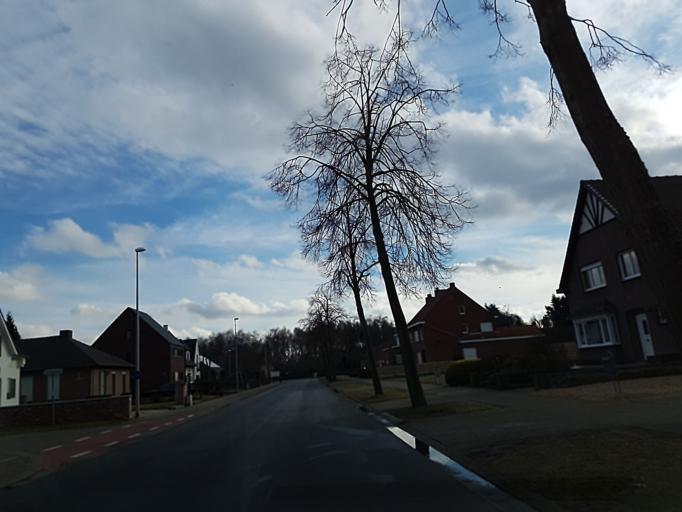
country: BE
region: Flanders
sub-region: Provincie Antwerpen
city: Dessel
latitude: 51.2349
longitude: 5.1085
